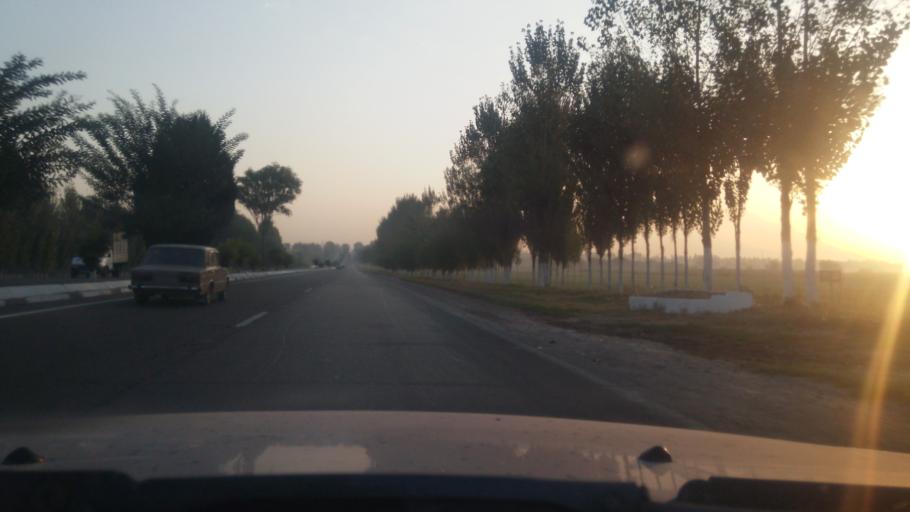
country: UZ
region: Toshkent
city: Yangiyul
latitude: 41.1303
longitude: 69.0082
